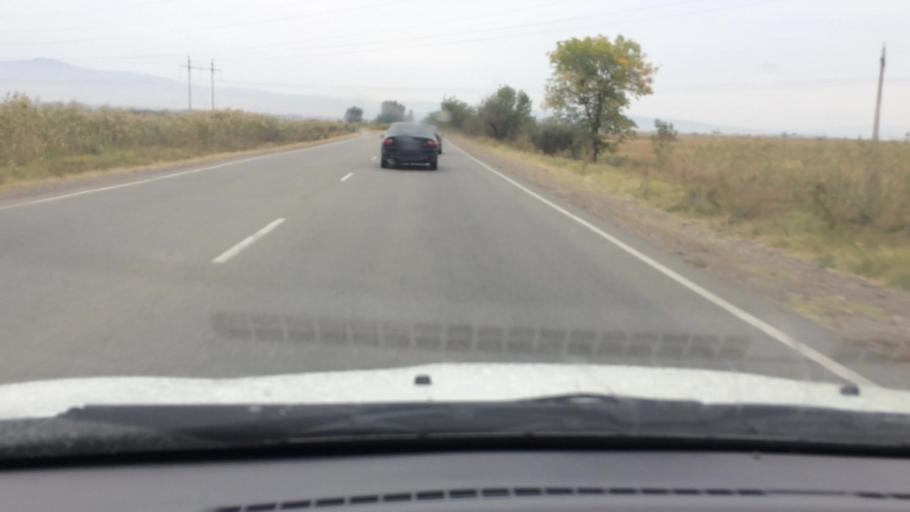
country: GE
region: Kvemo Kartli
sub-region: Marneuli
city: Marneuli
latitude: 41.5416
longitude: 44.7768
